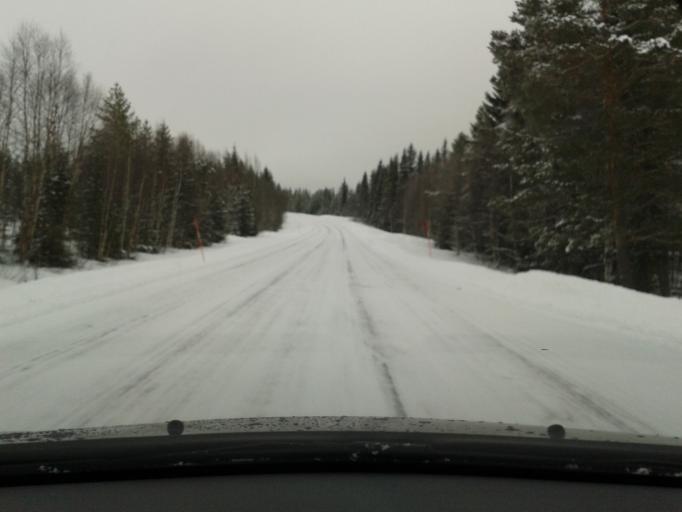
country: SE
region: Vaesterbotten
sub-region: Vilhelmina Kommun
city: Sjoberg
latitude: 64.8623
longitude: 15.8961
